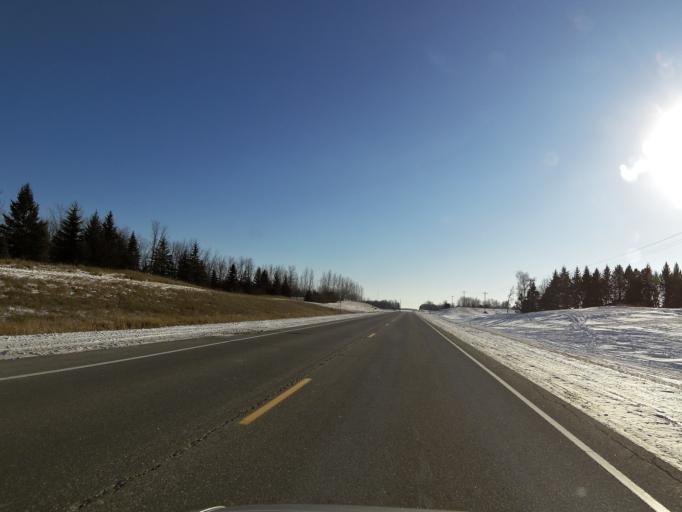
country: US
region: Minnesota
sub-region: Le Sueur County
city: New Prague
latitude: 44.5887
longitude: -93.5070
